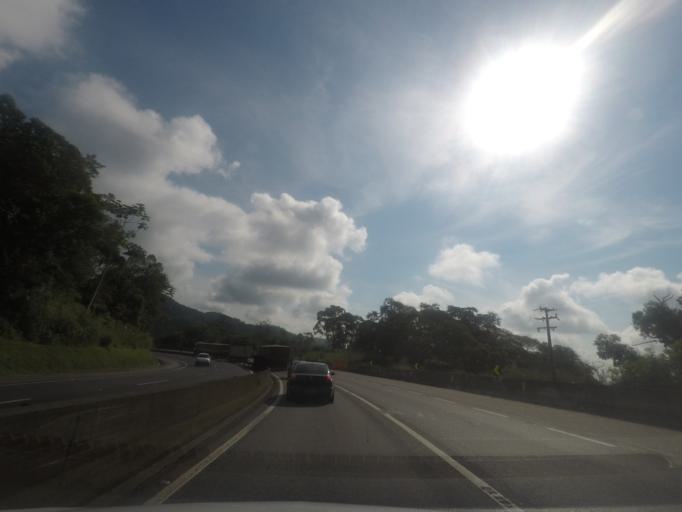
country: BR
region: Parana
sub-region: Antonina
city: Antonina
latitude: -25.5671
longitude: -48.8109
